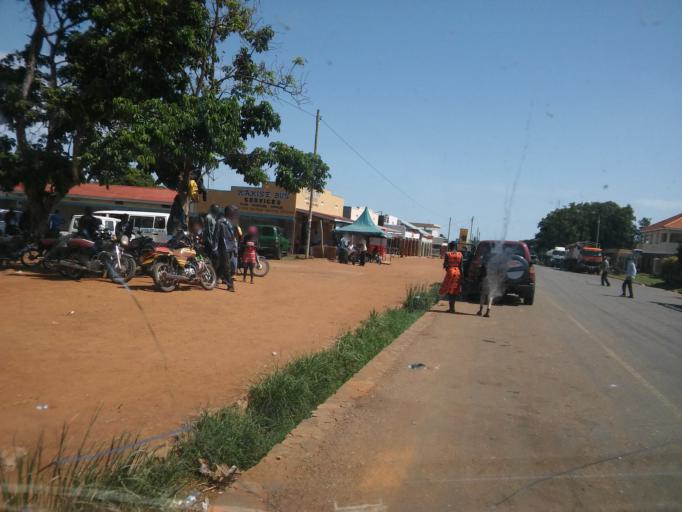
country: UG
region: Eastern Region
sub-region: Kumi District
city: Kumi
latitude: 1.4897
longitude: 33.9364
